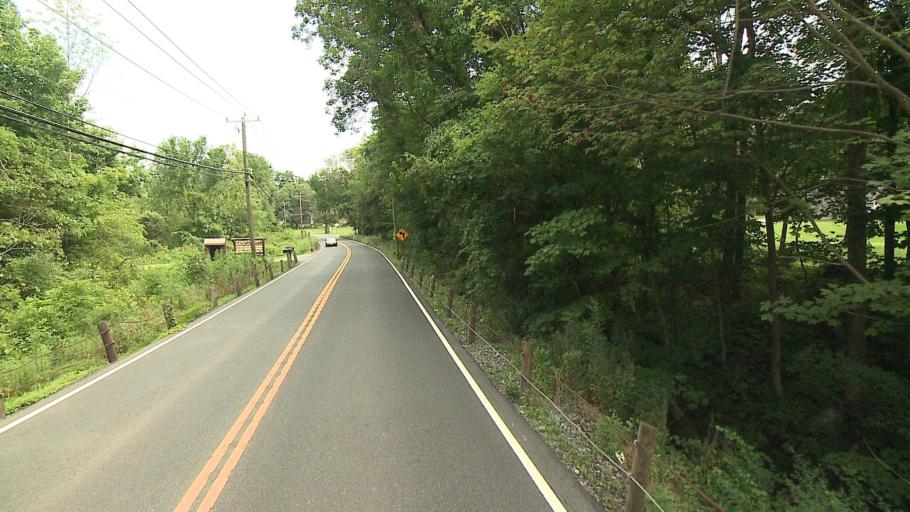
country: US
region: Connecticut
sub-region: Fairfield County
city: Sherman
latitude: 41.5018
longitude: -73.4695
